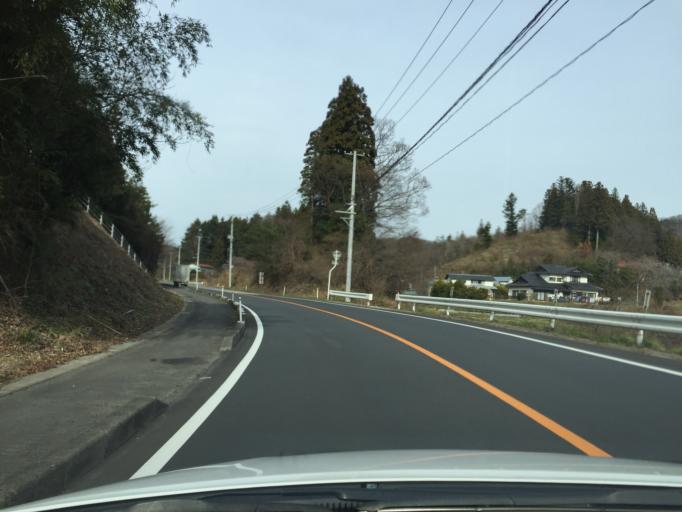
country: JP
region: Fukushima
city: Funehikimachi-funehiki
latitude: 37.3295
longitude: 140.6122
